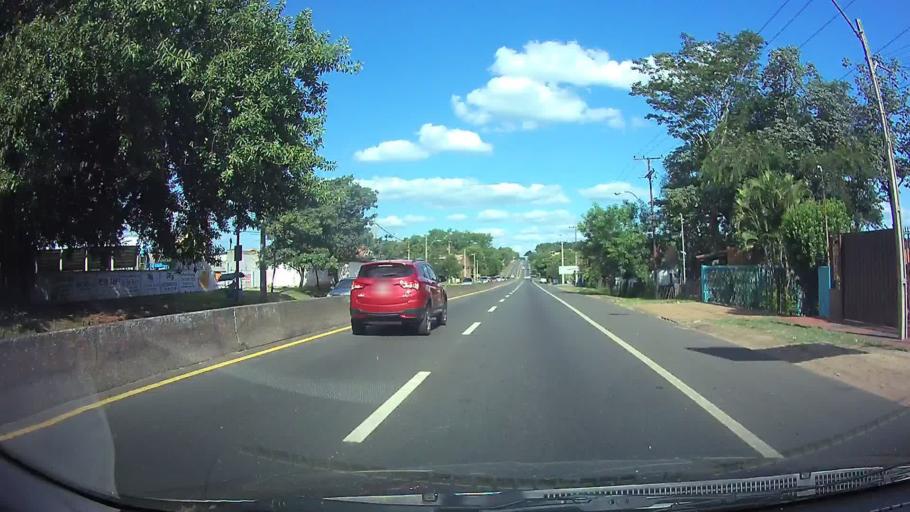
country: PY
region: Central
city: Itaugua
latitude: -25.3970
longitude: -57.3415
